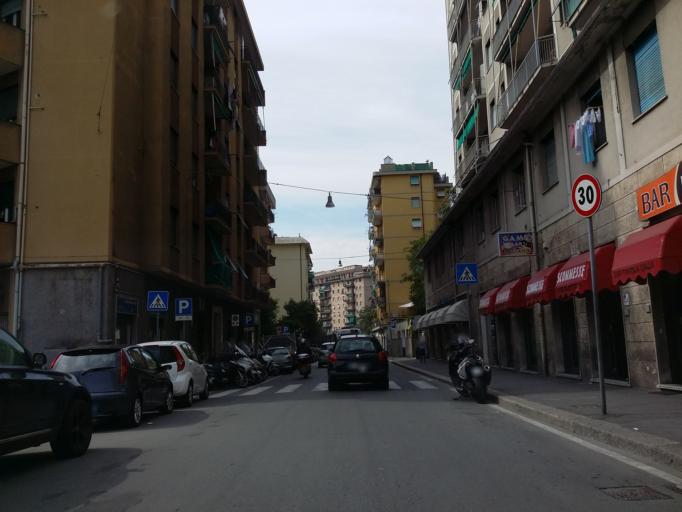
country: IT
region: Liguria
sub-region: Provincia di Genova
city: Piccarello
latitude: 44.4519
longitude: 8.9750
